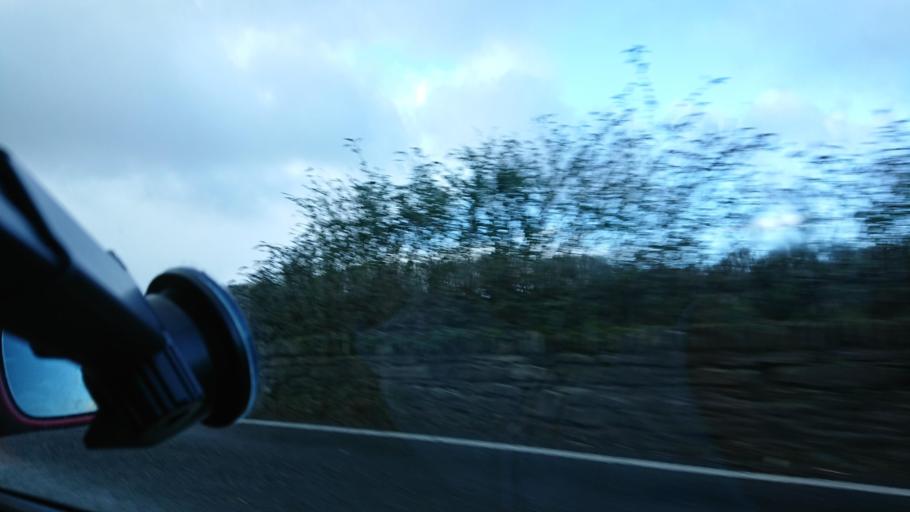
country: GB
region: England
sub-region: Cornwall
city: Looe
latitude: 50.3535
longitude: -4.4724
